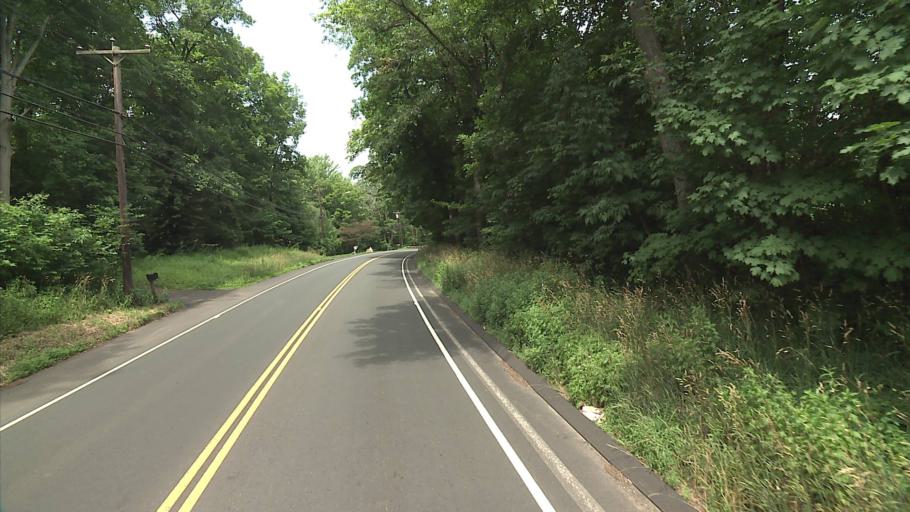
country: US
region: Connecticut
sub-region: New Haven County
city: North Branford
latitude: 41.3366
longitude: -72.7973
